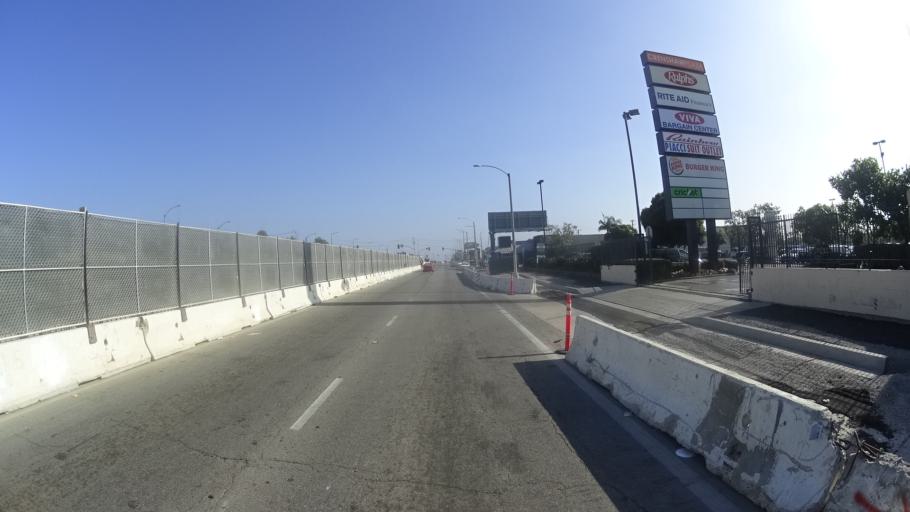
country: US
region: California
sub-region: Los Angeles County
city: View Park-Windsor Hills
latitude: 33.9875
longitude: -118.3307
